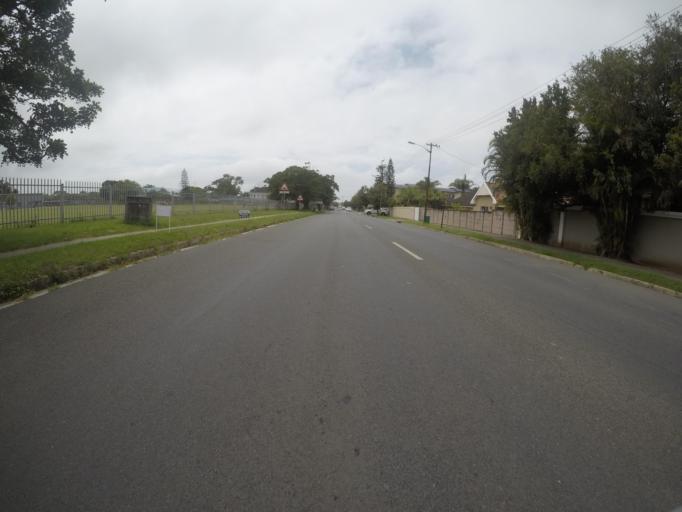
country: ZA
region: Eastern Cape
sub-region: Buffalo City Metropolitan Municipality
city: East London
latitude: -32.9848
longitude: 27.9245
